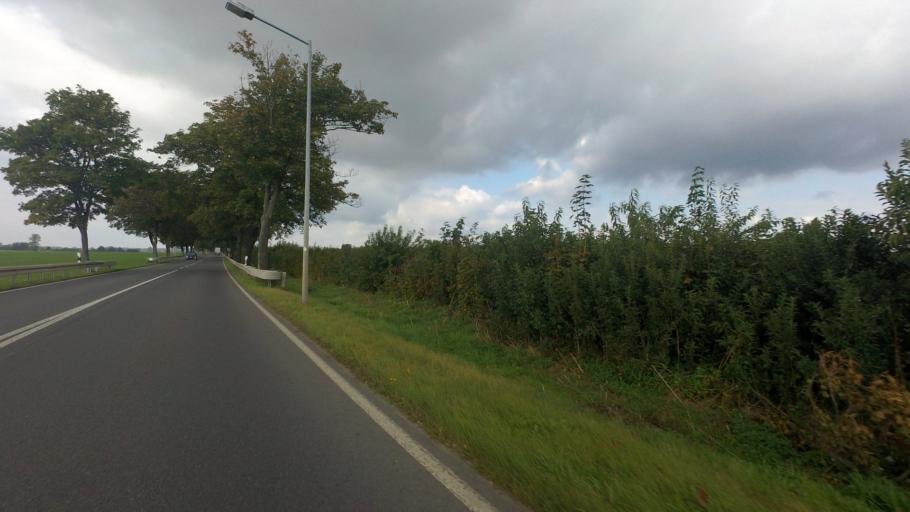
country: DE
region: Brandenburg
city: Plessa
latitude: 51.4659
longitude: 13.6033
